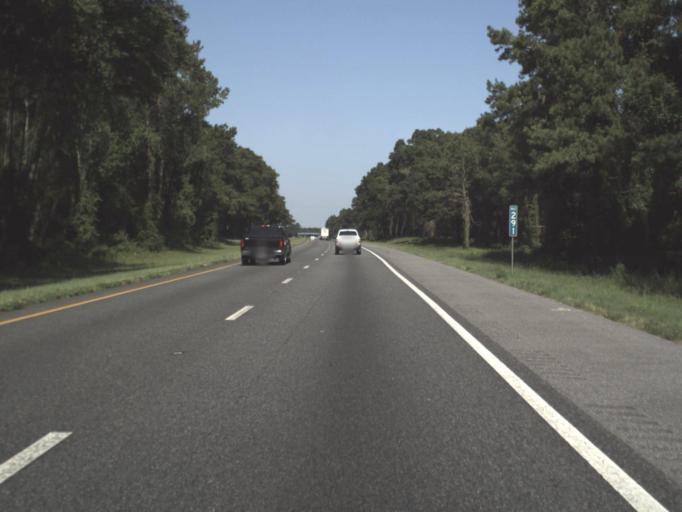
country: US
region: Florida
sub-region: Suwannee County
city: Wellborn
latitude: 30.2863
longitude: -82.8384
